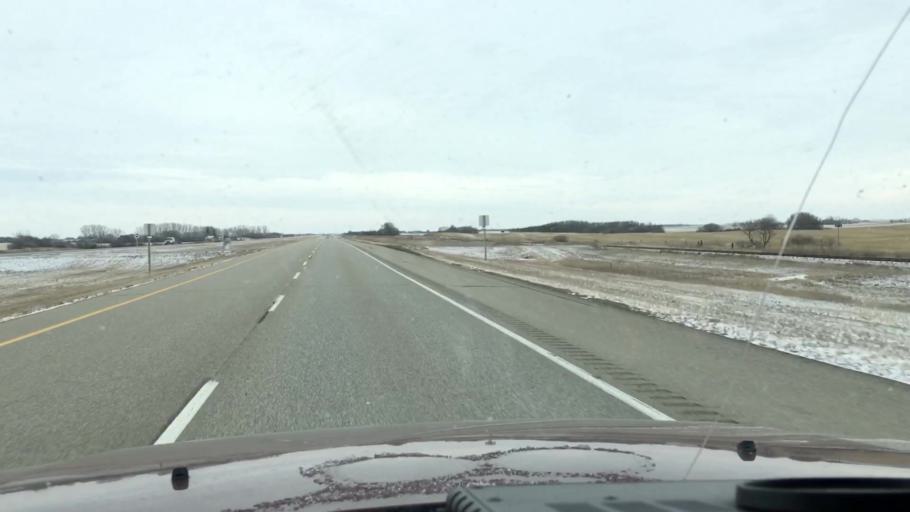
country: CA
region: Saskatchewan
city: Watrous
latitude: 51.3480
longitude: -106.1124
